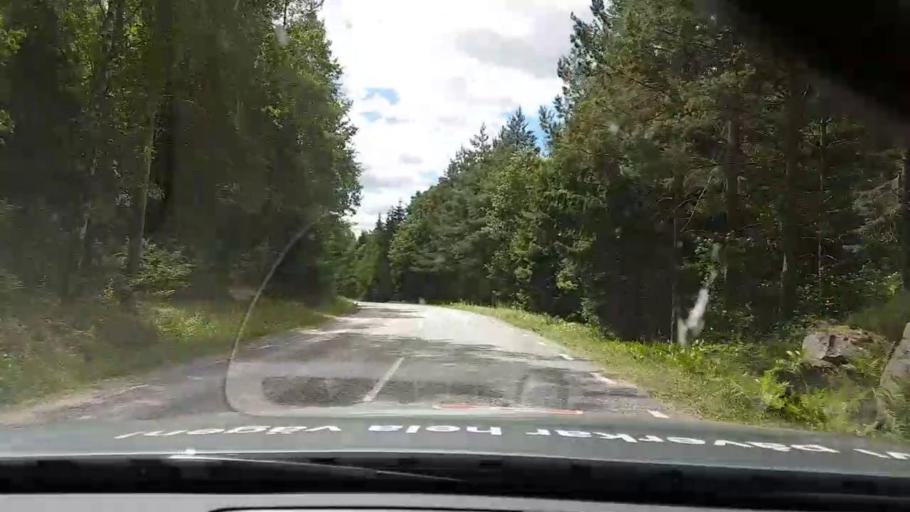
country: SE
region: Kalmar
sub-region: Vasterviks Kommun
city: Forserum
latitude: 58.0249
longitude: 16.5335
